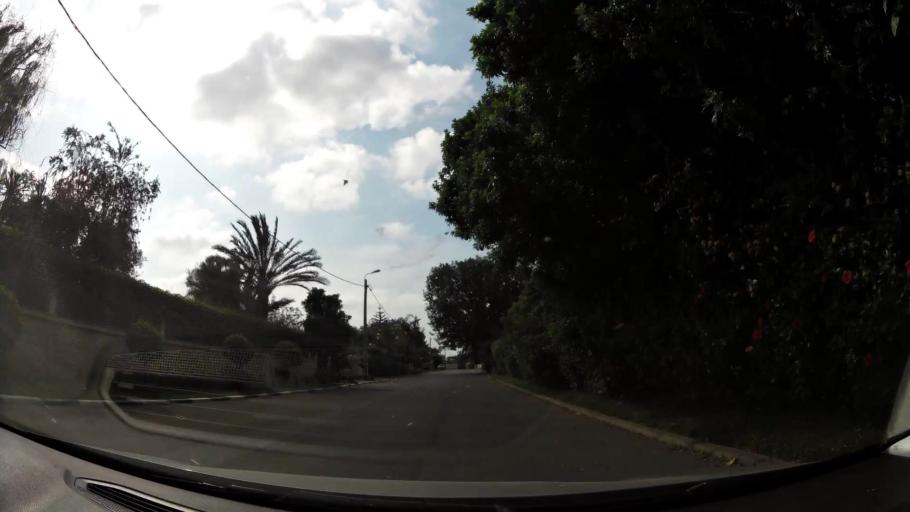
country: MA
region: Rabat-Sale-Zemmour-Zaer
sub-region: Rabat
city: Rabat
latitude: 33.9733
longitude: -6.8517
